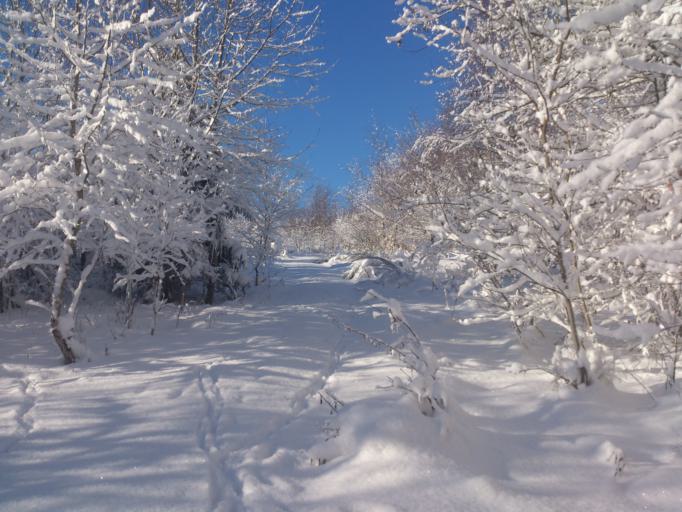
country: DE
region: Bavaria
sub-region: Upper Franconia
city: Stadtsteinach
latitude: 50.1999
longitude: 11.5045
